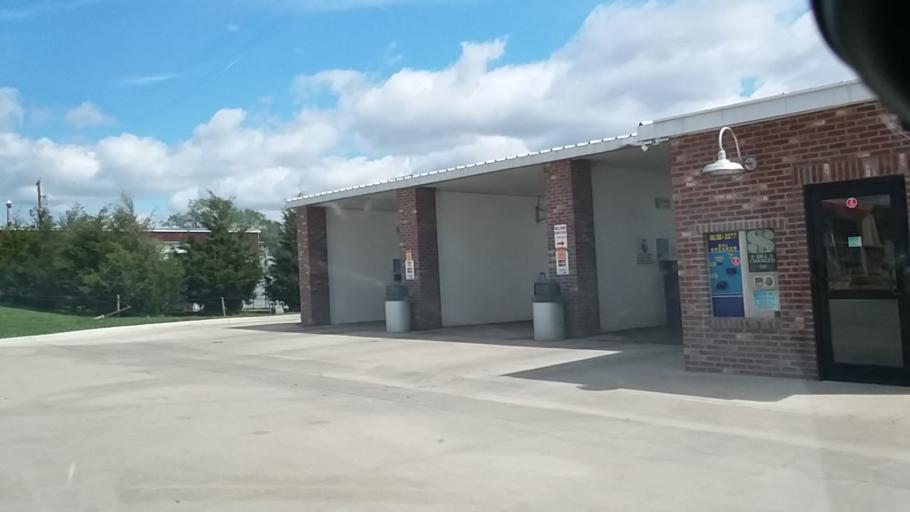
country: US
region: Kansas
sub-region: Douglas County
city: Lawrence
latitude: 38.9430
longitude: -95.2255
